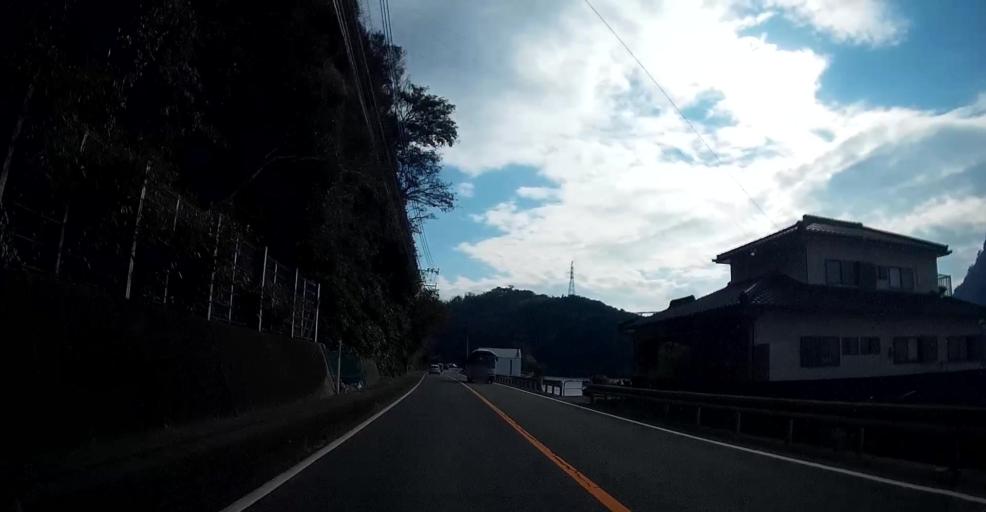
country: JP
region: Kumamoto
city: Yatsushiro
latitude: 32.6153
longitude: 130.4621
